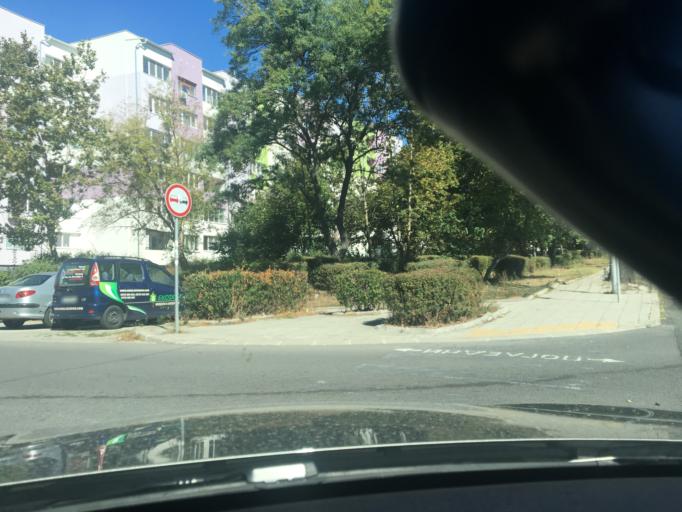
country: BG
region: Burgas
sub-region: Obshtina Burgas
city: Burgas
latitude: 42.5134
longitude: 27.4584
